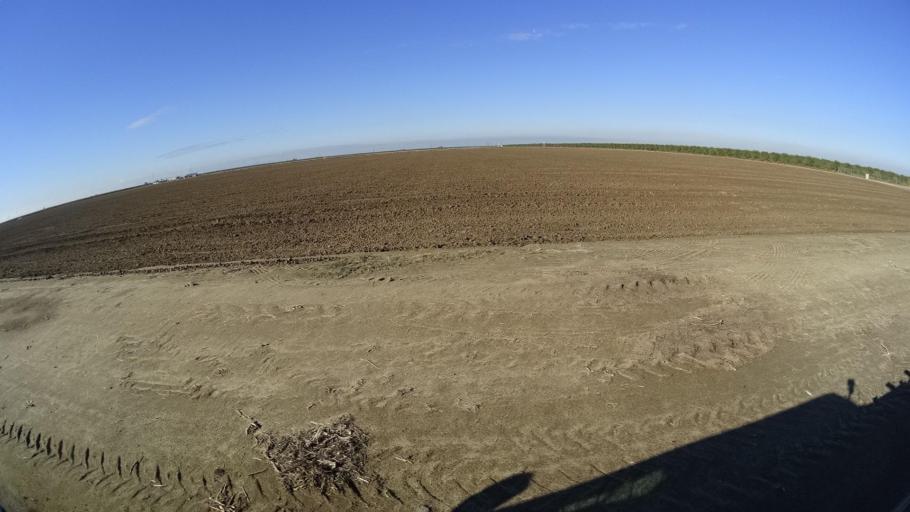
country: US
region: California
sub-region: Kern County
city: McFarland
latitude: 35.7097
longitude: -119.2764
